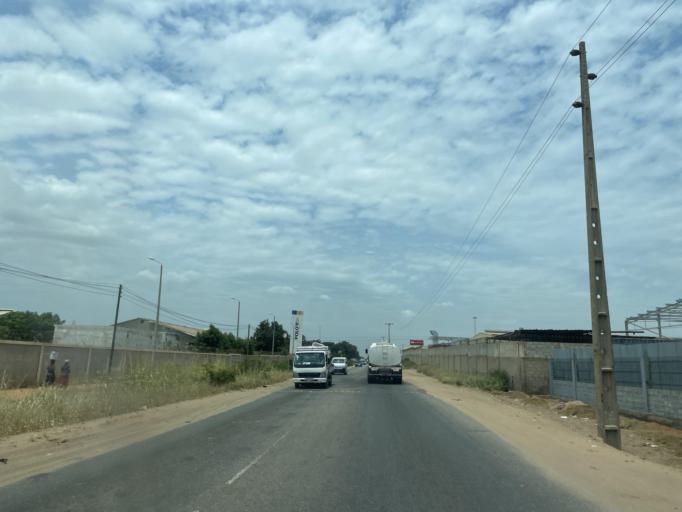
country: AO
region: Luanda
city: Luanda
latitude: -8.9299
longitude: 13.3946
